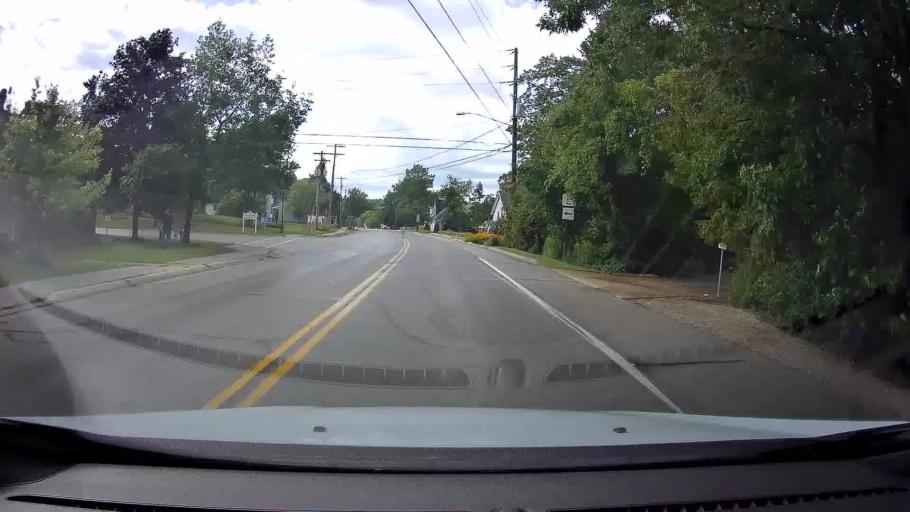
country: US
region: Wisconsin
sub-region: Door County
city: Sturgeon Bay
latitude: 45.0548
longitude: -87.2805
